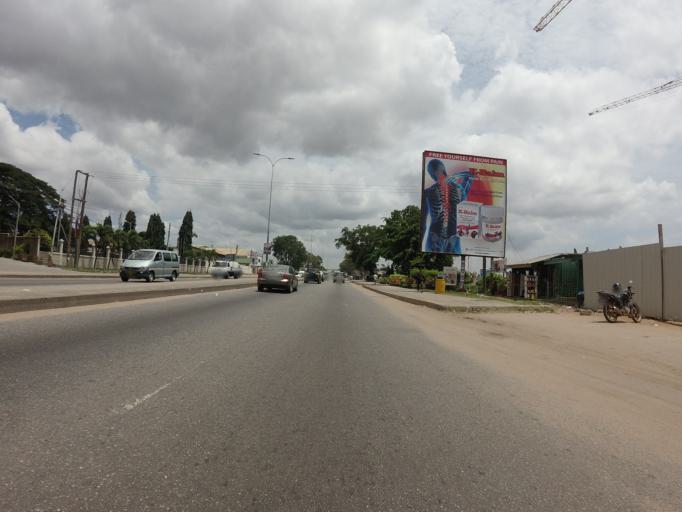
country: GH
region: Greater Accra
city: Gbawe
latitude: 5.5764
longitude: -0.2742
